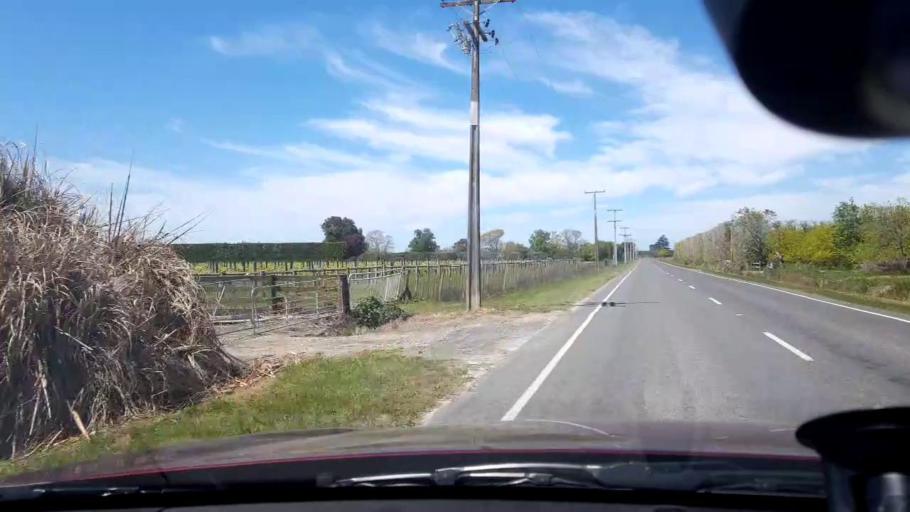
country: NZ
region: Gisborne
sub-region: Gisborne District
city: Gisborne
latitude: -38.6322
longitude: 177.9281
